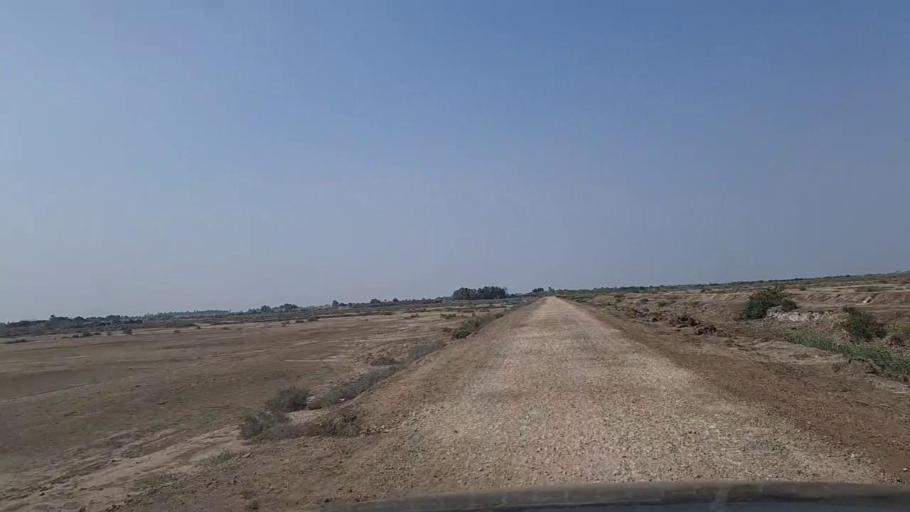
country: PK
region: Sindh
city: Gharo
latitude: 24.7019
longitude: 67.5891
